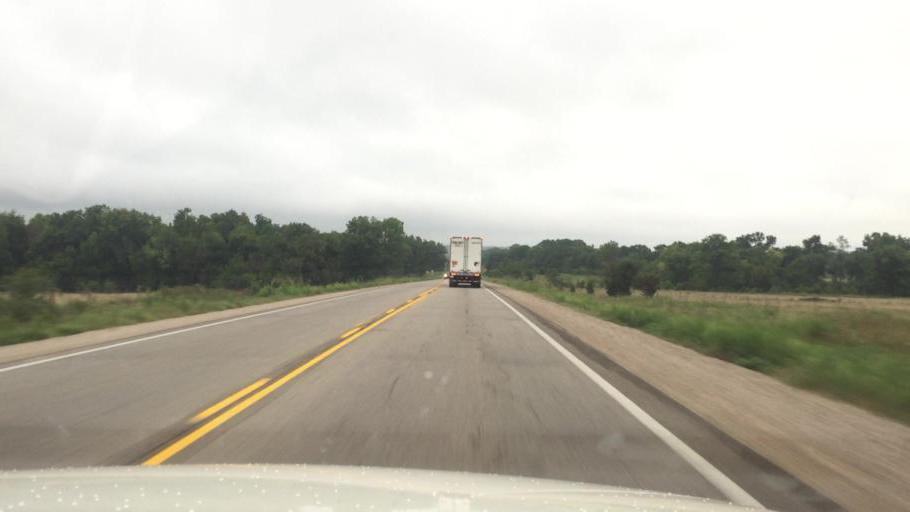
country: US
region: Kansas
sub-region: Montgomery County
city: Cherryvale
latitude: 37.1889
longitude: -95.5799
